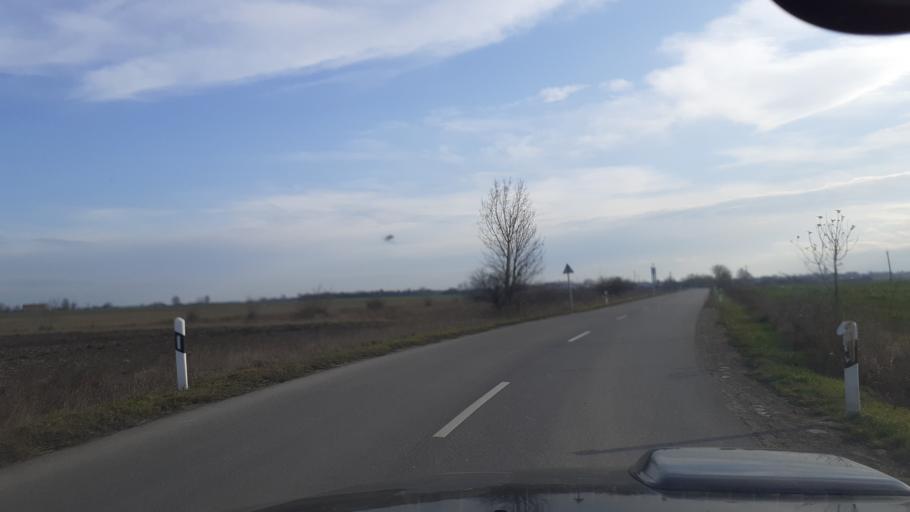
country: HU
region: Bacs-Kiskun
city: Kunszentmiklos
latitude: 47.0480
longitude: 19.1177
